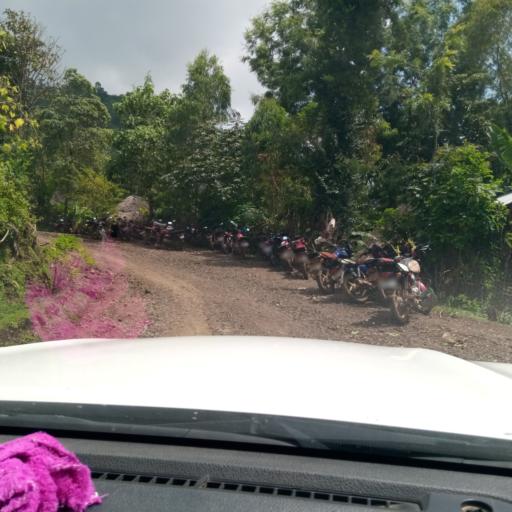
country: ET
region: Southern Nations, Nationalities, and People's Region
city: Arba Minch'
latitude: 6.3123
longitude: 37.3716
